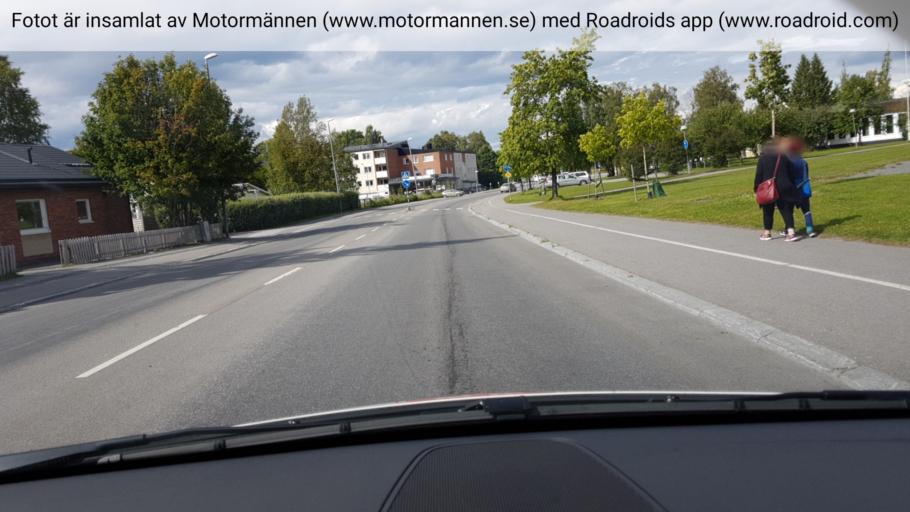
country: SE
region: Jaemtland
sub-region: OEstersunds Kommun
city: Ostersund
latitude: 63.1742
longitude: 14.6593
